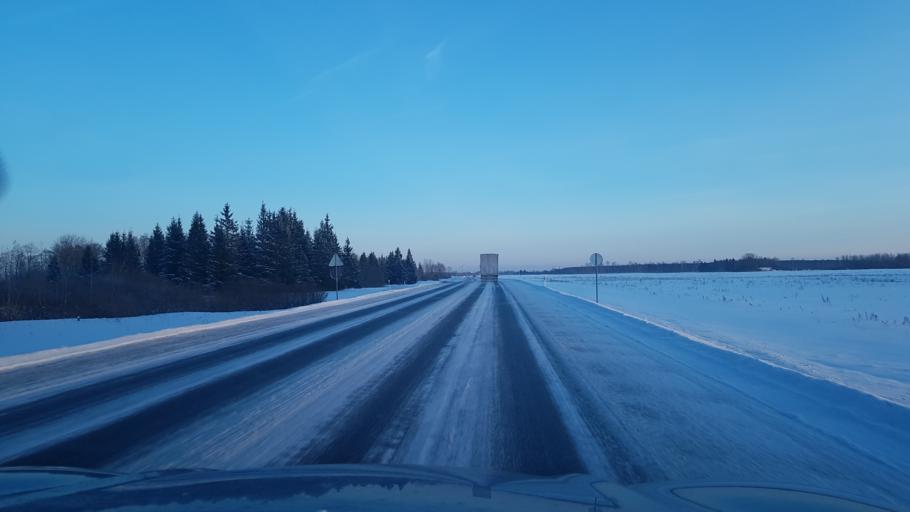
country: EE
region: Ida-Virumaa
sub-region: Narva-Joesuu linn
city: Narva-Joesuu
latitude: 59.3938
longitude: 28.0832
